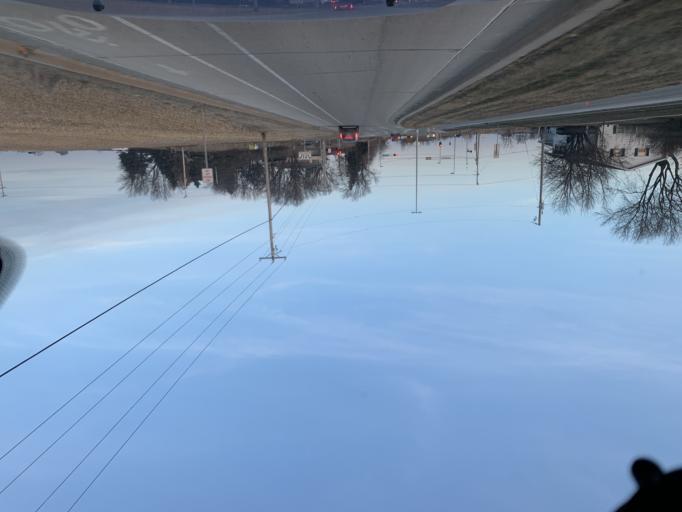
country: US
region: Wisconsin
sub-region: Dane County
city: Middleton
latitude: 43.0588
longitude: -89.5520
